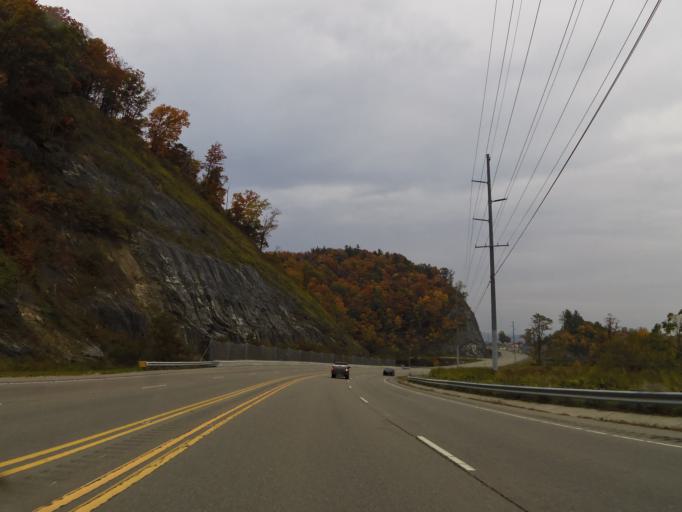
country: US
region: North Carolina
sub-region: Watauga County
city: Blowing Rock
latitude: 36.1024
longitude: -81.6441
